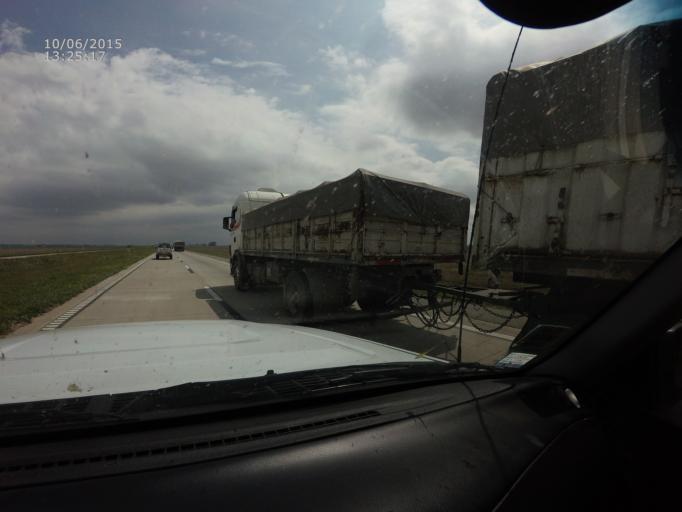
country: AR
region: Cordoba
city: Marcos Juarez
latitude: -32.6535
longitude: -62.1571
